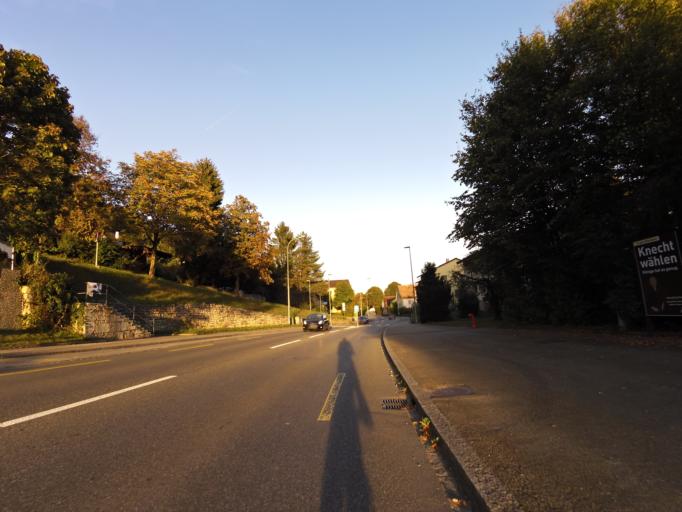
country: CH
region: Aargau
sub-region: Bezirk Aarau
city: Aarau
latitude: 47.3954
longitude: 8.0312
